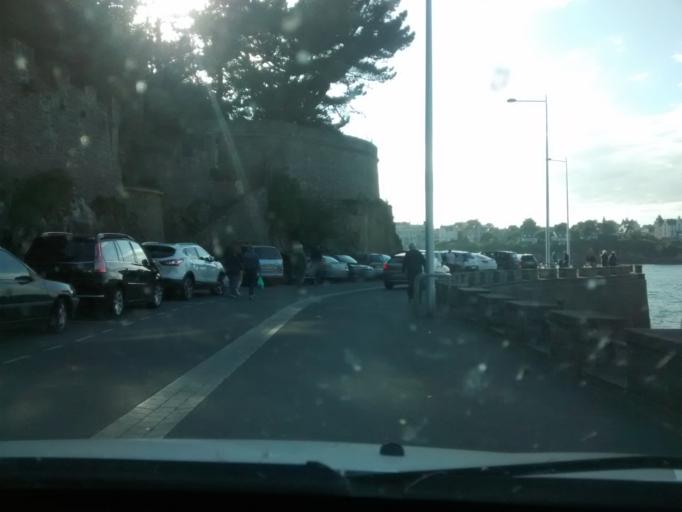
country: FR
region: Brittany
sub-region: Departement d'Ille-et-Vilaine
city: Dinard
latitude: 48.6369
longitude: -2.0496
